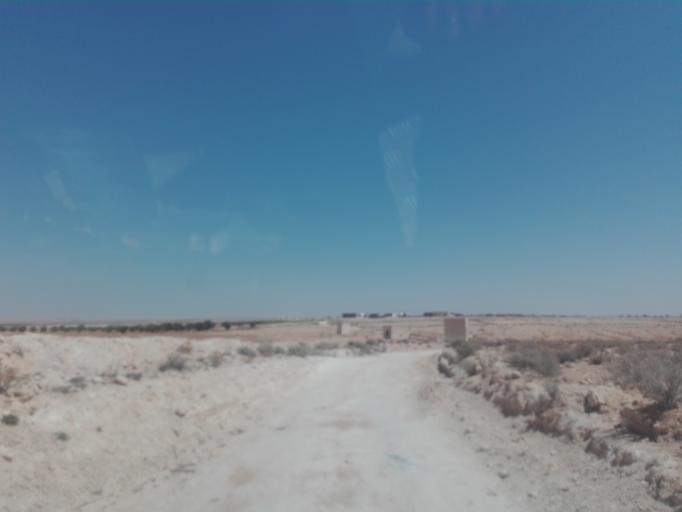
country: TN
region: Safaqis
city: Skhira
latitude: 34.3872
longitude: 9.9237
